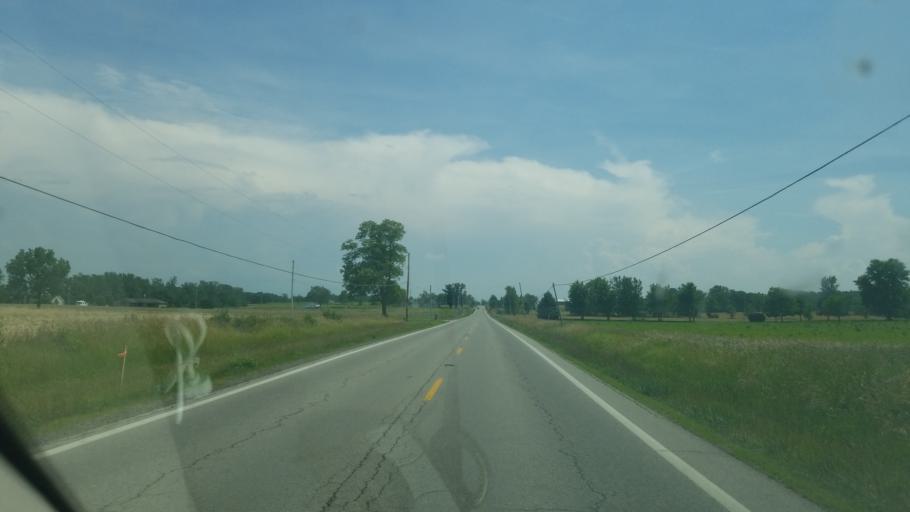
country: US
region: Ohio
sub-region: Logan County
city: Northwood
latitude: 40.4931
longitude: -83.7419
